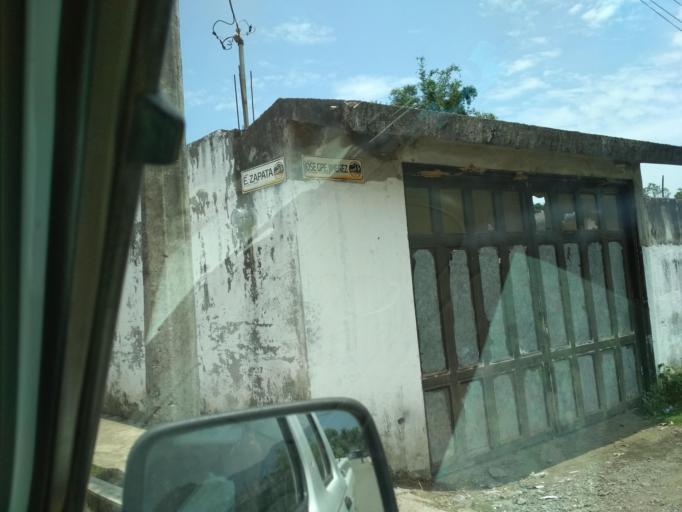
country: MX
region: Veracruz
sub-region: Mariano Escobedo
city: Mariano Escobedo
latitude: 18.9114
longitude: -97.1275
